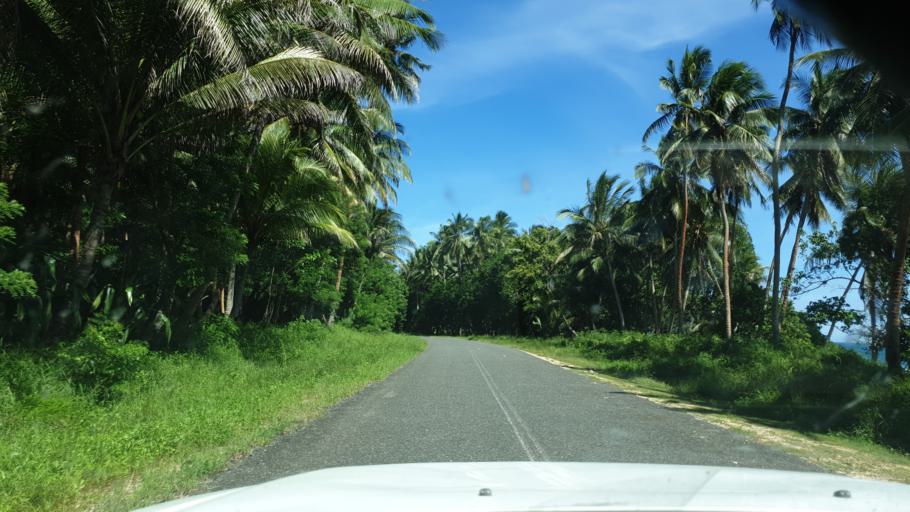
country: PG
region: Madang
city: Madang
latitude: -4.4978
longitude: 145.4570
